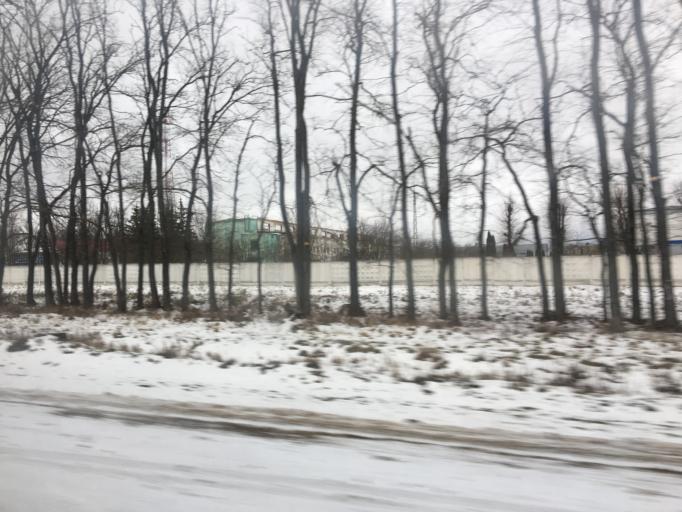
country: RU
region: Tula
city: Pervomayskiy
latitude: 54.0385
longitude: 37.5255
